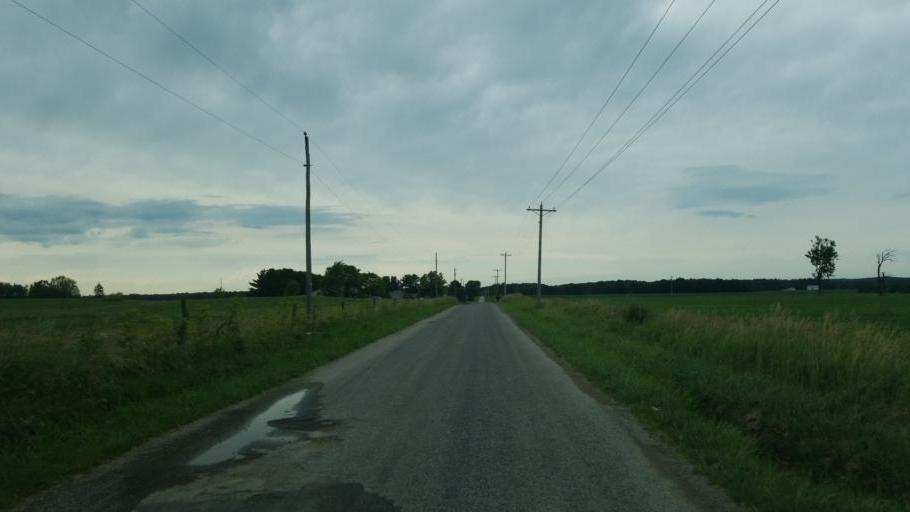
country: US
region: Ohio
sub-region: Ashland County
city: Ashland
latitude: 40.9509
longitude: -82.4074
